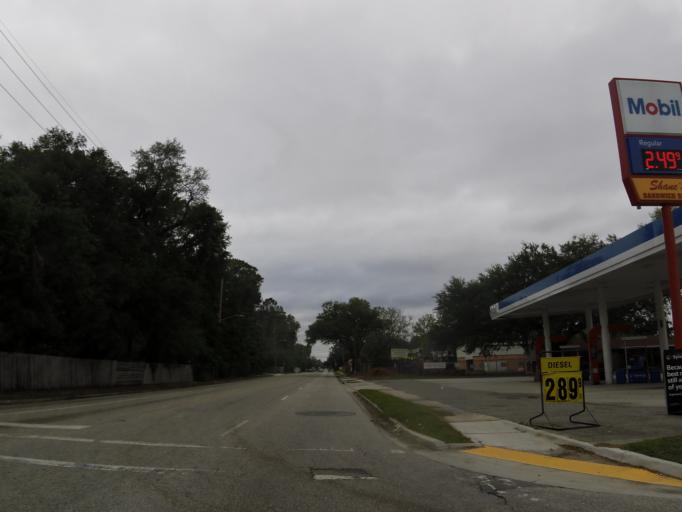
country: US
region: Florida
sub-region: Duval County
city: Jacksonville
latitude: 30.2676
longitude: -81.6335
